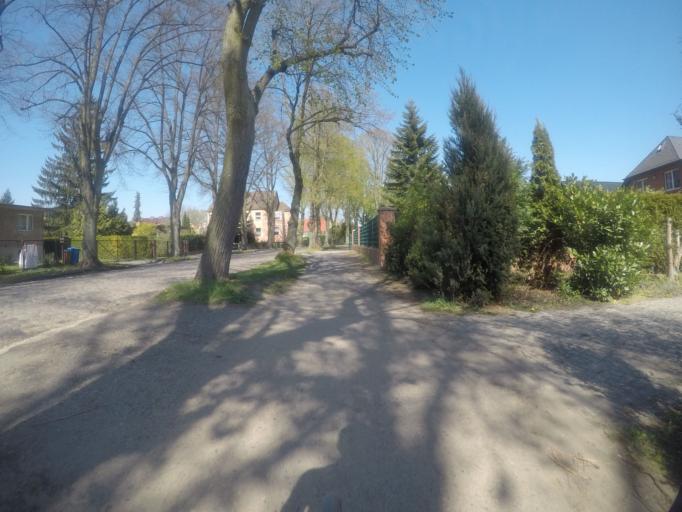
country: DE
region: Berlin
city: Buch
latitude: 52.6542
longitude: 13.5292
